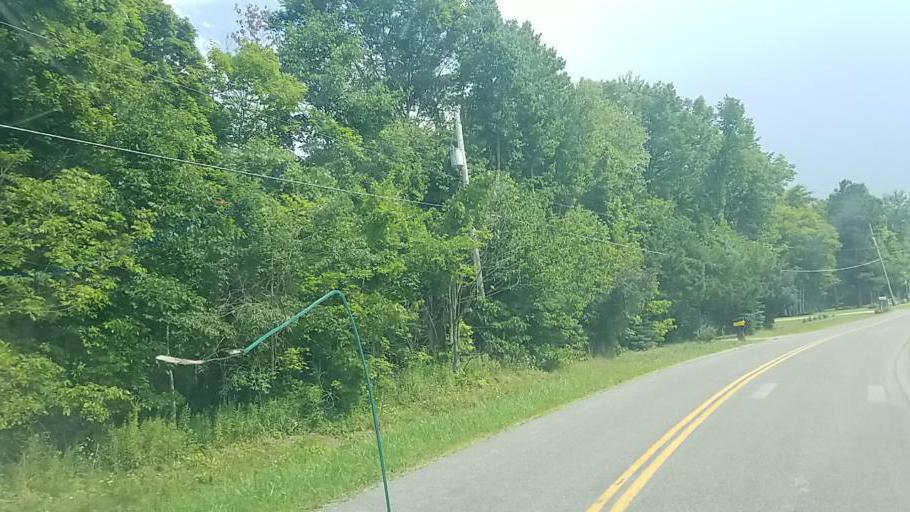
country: US
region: Ohio
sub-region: Medina County
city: Westfield Center
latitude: 41.1055
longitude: -81.9623
